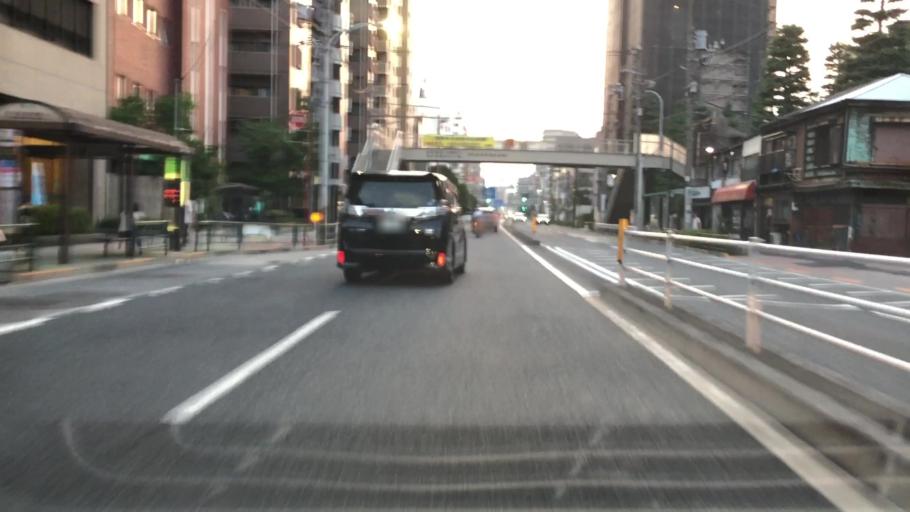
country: JP
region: Saitama
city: Soka
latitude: 35.7349
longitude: 139.7842
